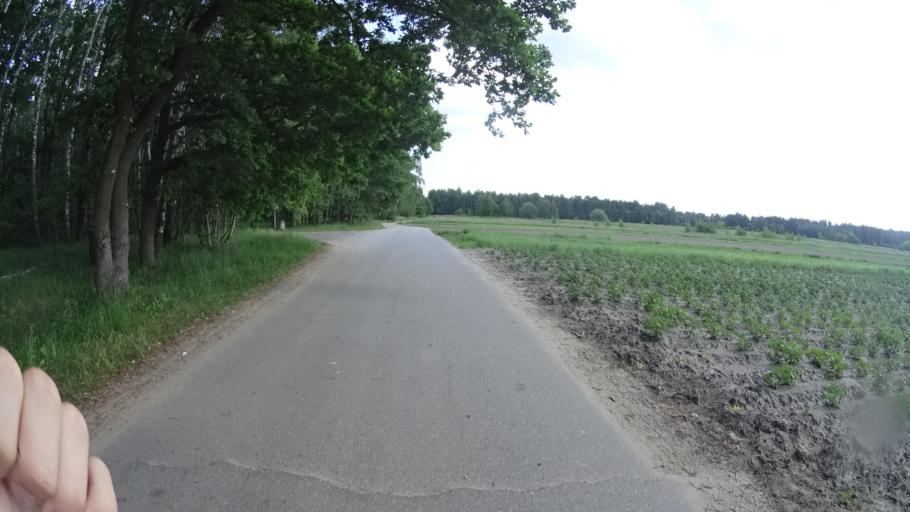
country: PL
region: Masovian Voivodeship
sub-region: Warszawa
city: Kabaty
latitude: 52.1122
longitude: 21.0870
